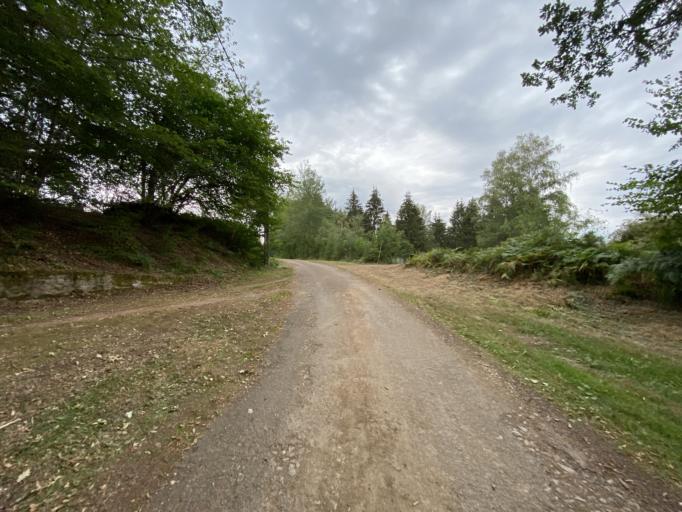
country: FR
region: Bourgogne
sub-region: Departement de la Cote-d'Or
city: Saulieu
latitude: 47.2717
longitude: 4.1430
